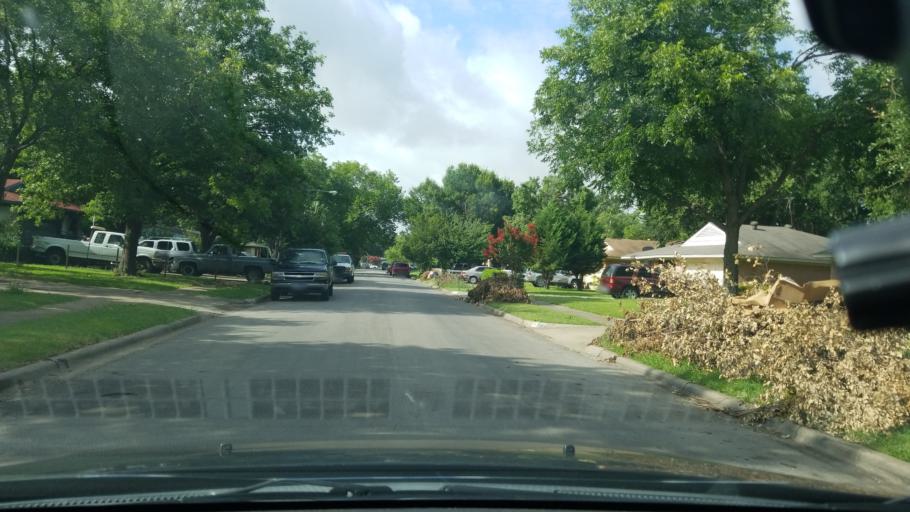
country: US
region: Texas
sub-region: Dallas County
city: Mesquite
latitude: 32.8167
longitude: -96.6766
